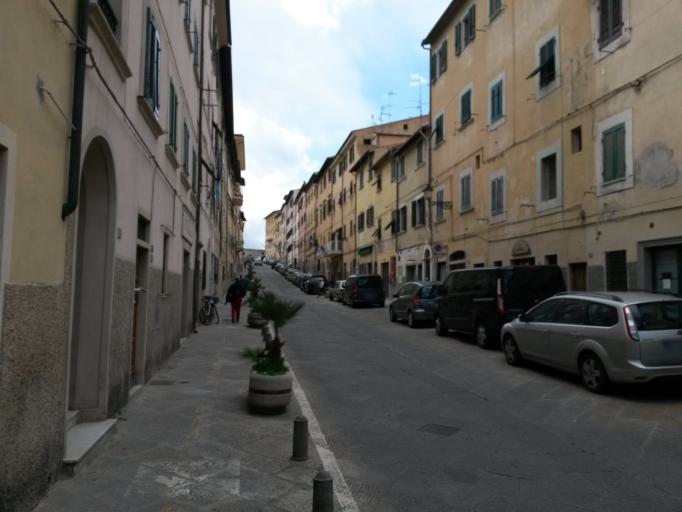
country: IT
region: Tuscany
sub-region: Provincia di Livorno
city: Portoferraio
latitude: 42.8147
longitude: 10.3296
